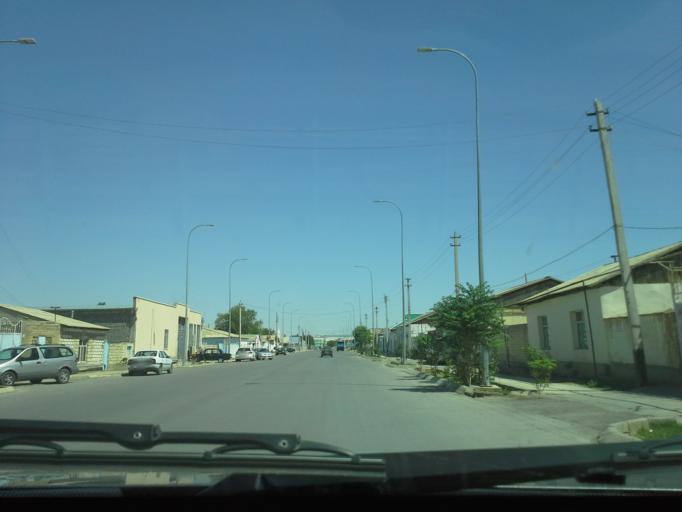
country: TM
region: Balkan
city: Serdar
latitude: 38.9758
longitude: 56.2675
